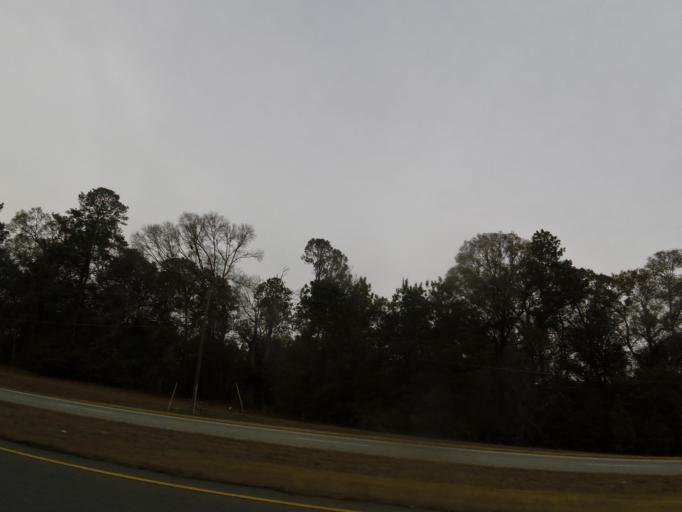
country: US
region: Georgia
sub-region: Thomas County
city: Thomasville
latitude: 30.8784
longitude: -84.0524
